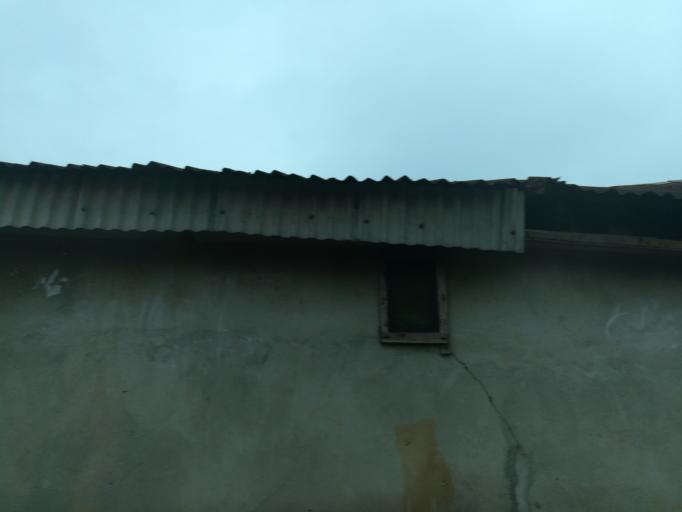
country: NG
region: Rivers
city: Port Harcourt
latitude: 4.8174
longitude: 7.0189
